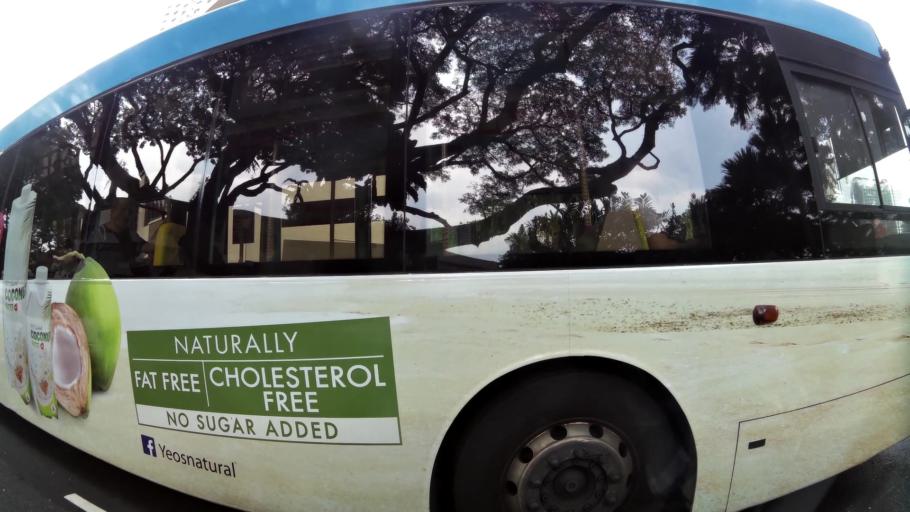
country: SG
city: Singapore
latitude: 1.2860
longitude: 103.8333
